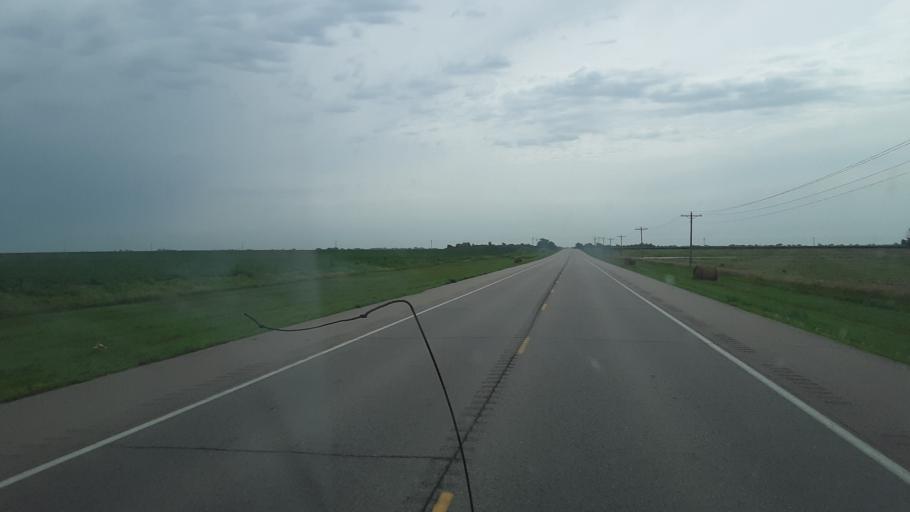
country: US
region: Kansas
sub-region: Stafford County
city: Saint John
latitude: 37.9563
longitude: -98.8664
